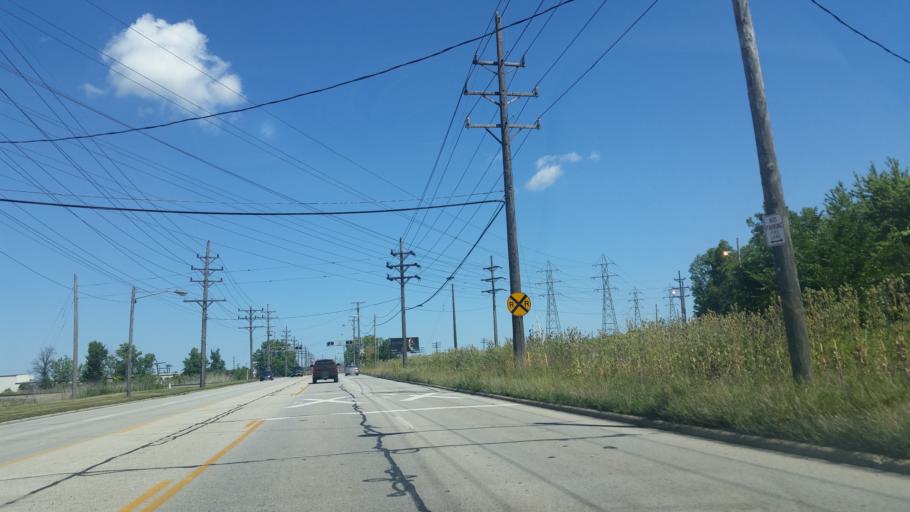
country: US
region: Ohio
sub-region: Cuyahoga County
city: Brook Park
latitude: 41.4094
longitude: -81.7840
